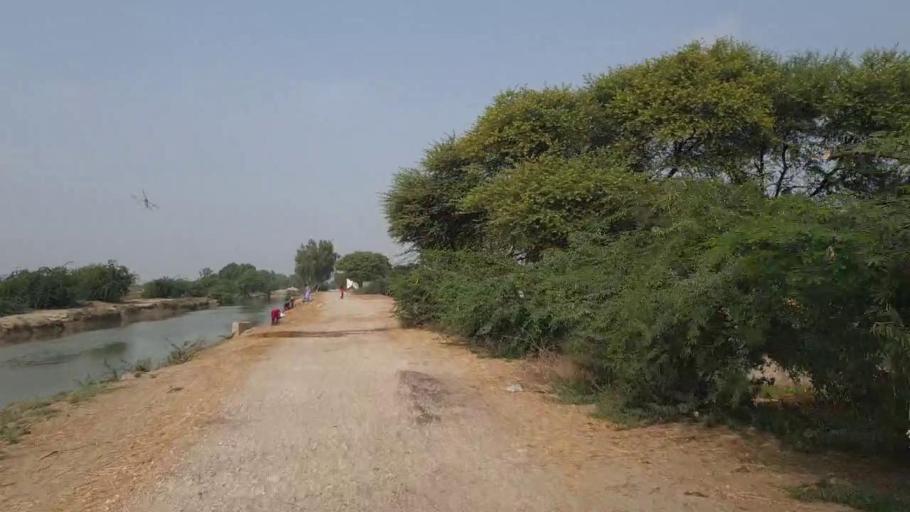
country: PK
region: Sindh
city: Kario
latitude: 24.8765
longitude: 68.5151
